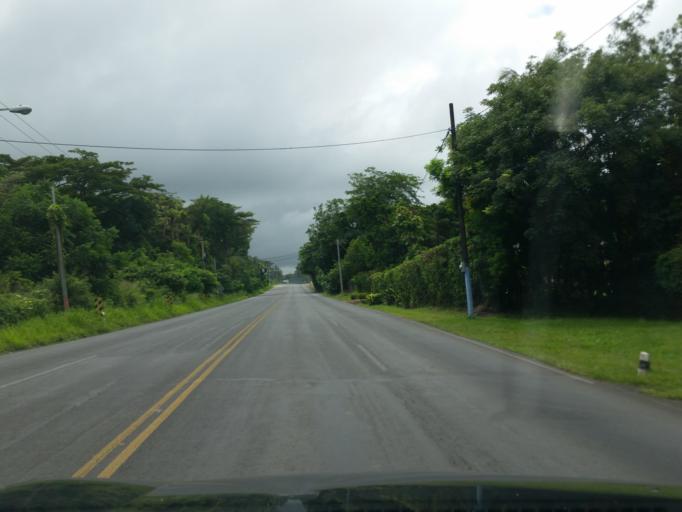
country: NI
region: Managua
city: El Crucero
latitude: 12.0614
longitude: -86.3187
